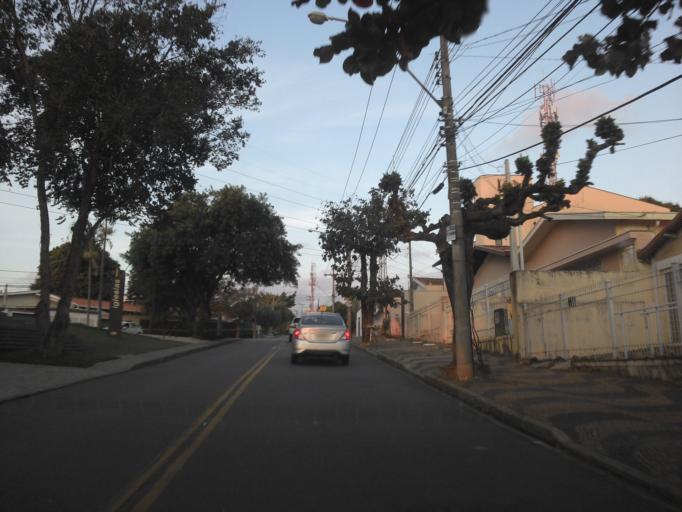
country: BR
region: Sao Paulo
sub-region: Campinas
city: Campinas
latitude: -22.8911
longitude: -47.0388
